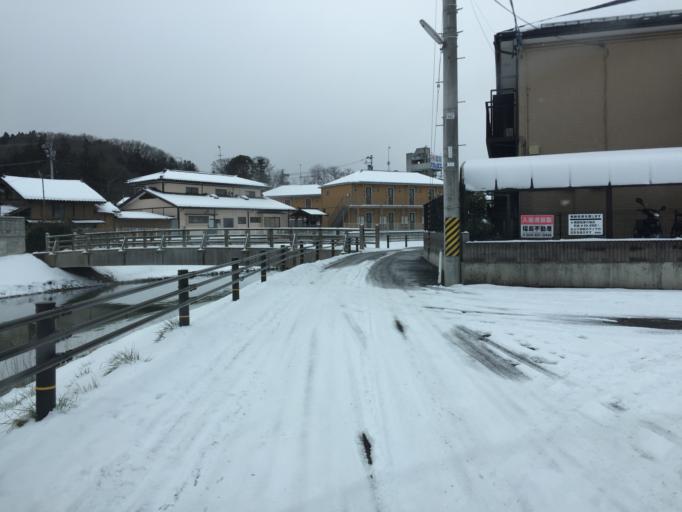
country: JP
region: Fukushima
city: Fukushima-shi
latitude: 37.7236
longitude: 140.4618
